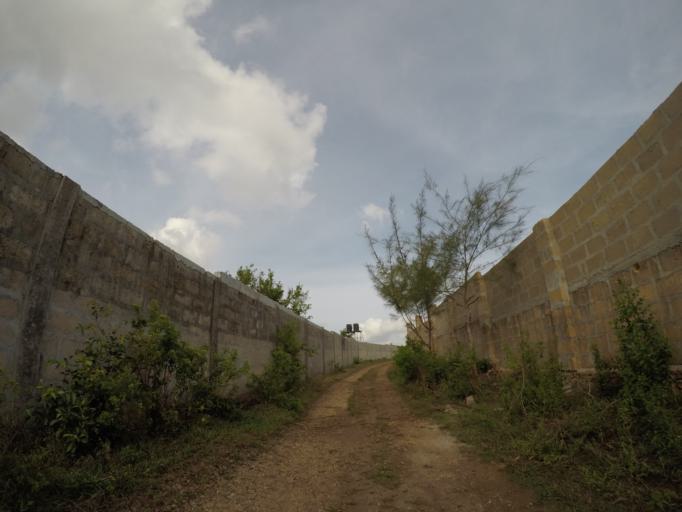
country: TZ
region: Zanzibar Central/South
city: Koani
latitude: -6.2343
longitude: 39.3176
